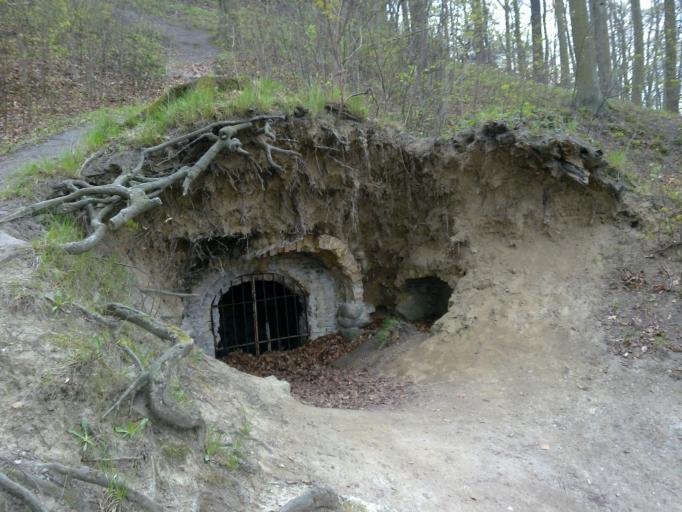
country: PL
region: Pomeranian Voivodeship
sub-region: Gdansk
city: Gdansk
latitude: 54.3217
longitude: 18.6264
